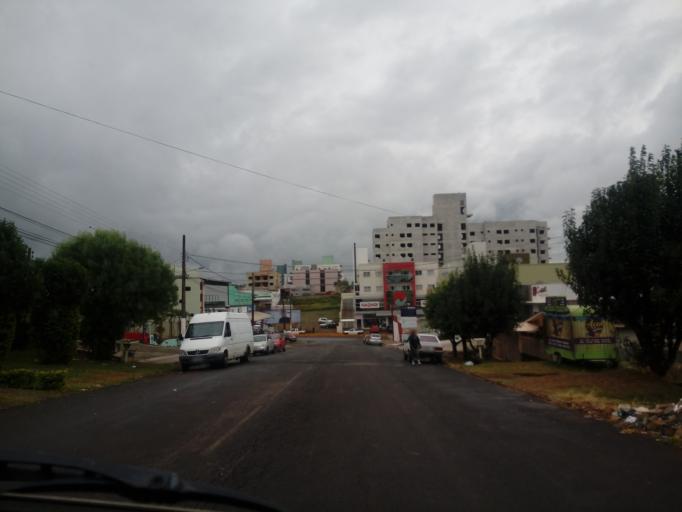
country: BR
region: Santa Catarina
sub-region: Chapeco
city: Chapeco
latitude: -27.0968
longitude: -52.6717
